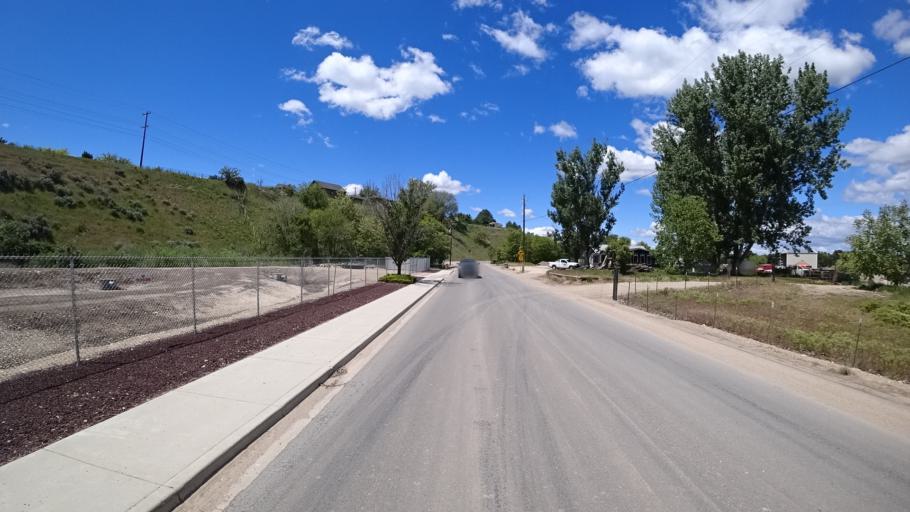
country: US
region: Idaho
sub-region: Ada County
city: Eagle
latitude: 43.6629
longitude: -116.3262
